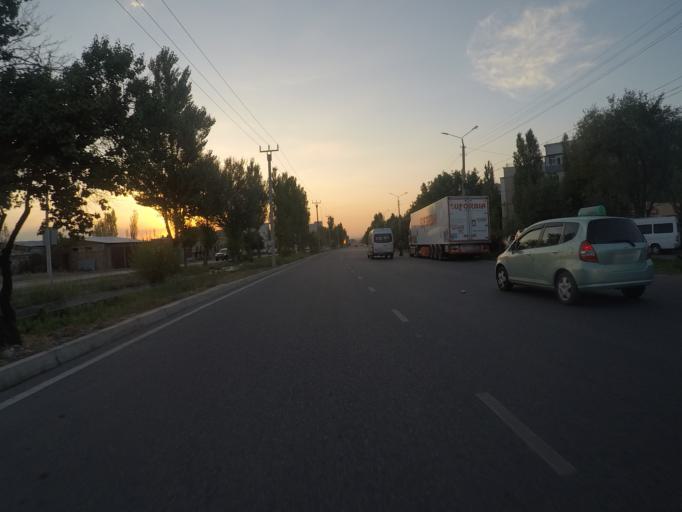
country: KG
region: Chuy
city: Bishkek
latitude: 42.8114
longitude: 74.6341
